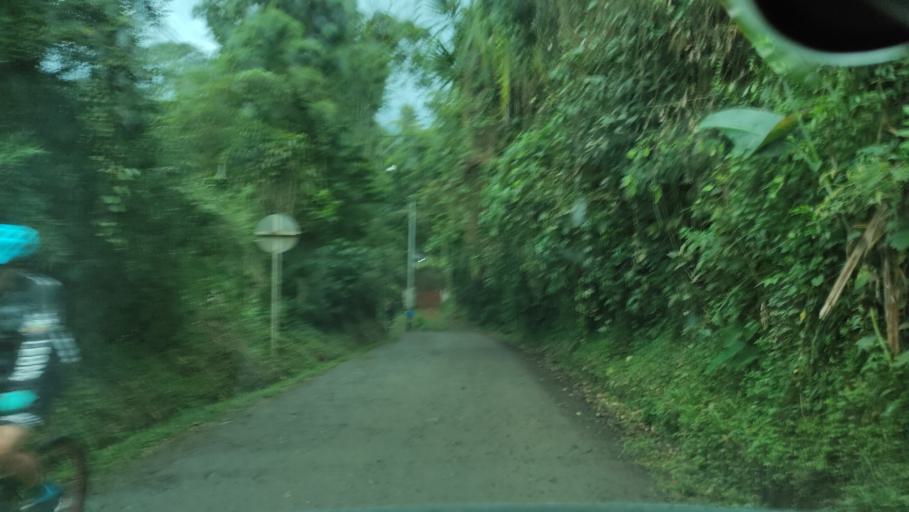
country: CO
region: Valle del Cauca
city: Jamundi
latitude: 3.3253
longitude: -76.6309
